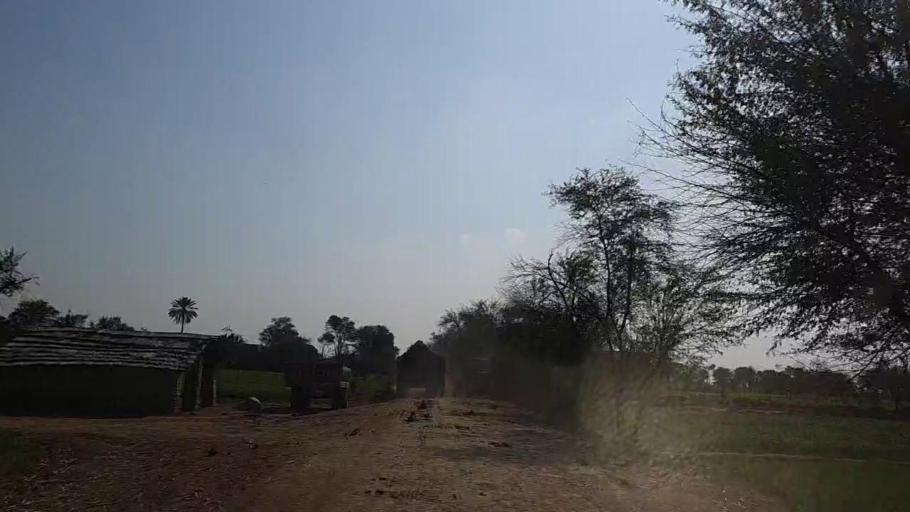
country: PK
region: Sindh
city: Daur
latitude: 26.4282
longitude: 68.2369
